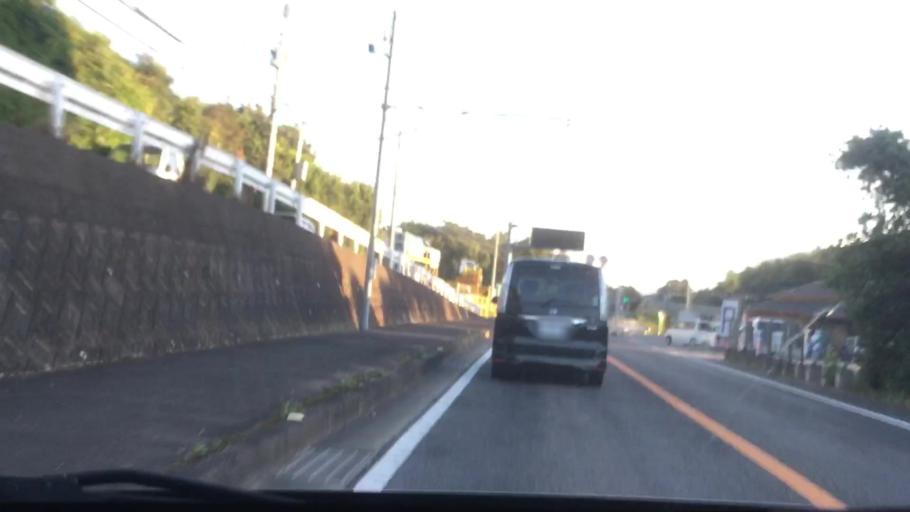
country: JP
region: Nagasaki
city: Sasebo
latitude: 33.0670
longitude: 129.7641
